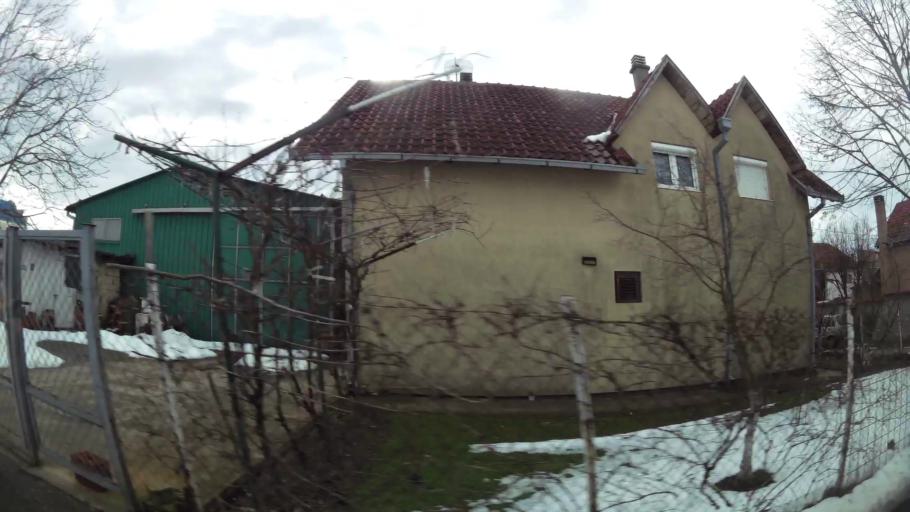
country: RS
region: Central Serbia
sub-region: Belgrade
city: Surcin
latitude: 44.8009
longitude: 20.3106
